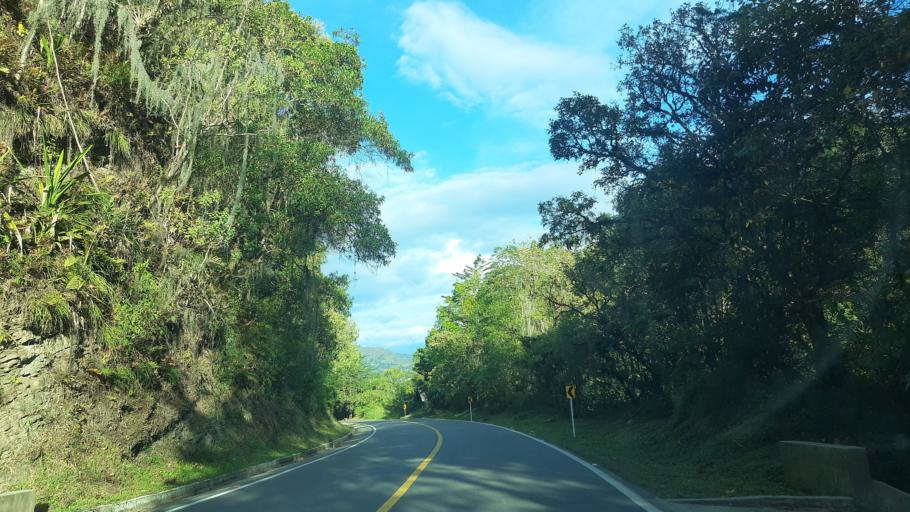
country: CO
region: Cundinamarca
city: Macheta
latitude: 5.0755
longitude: -73.5694
